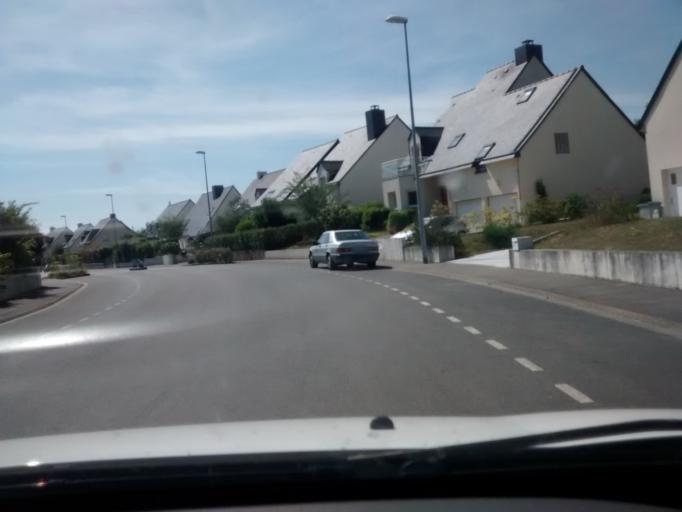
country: FR
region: Brittany
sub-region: Departement d'Ille-et-Vilaine
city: Cesson-Sevigne
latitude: 48.1079
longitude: -1.6093
